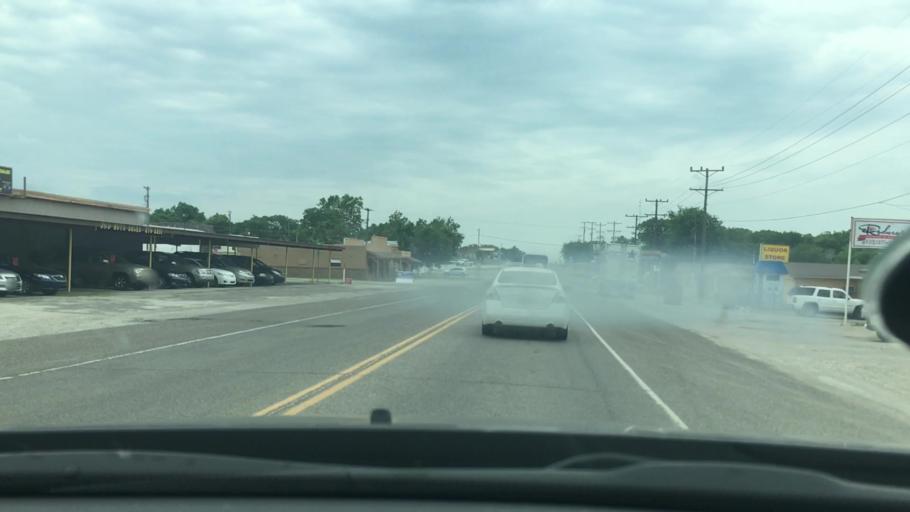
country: US
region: Oklahoma
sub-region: Love County
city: Marietta
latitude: 33.9397
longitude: -97.1263
